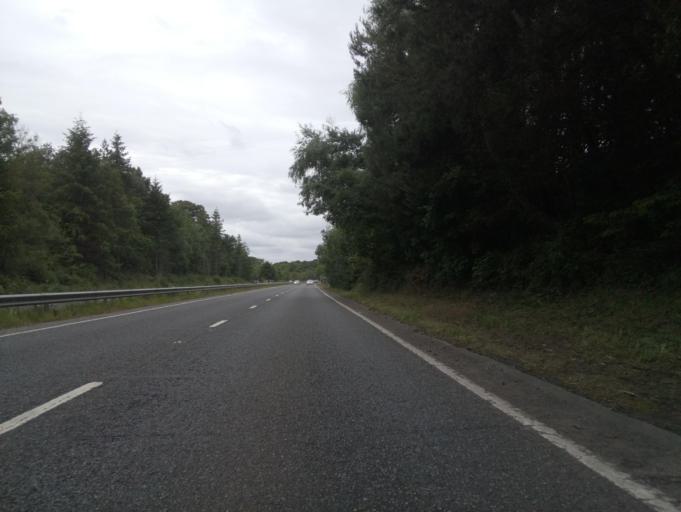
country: GB
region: England
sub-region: Devon
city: Chudleigh
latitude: 50.5762
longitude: -3.5960
